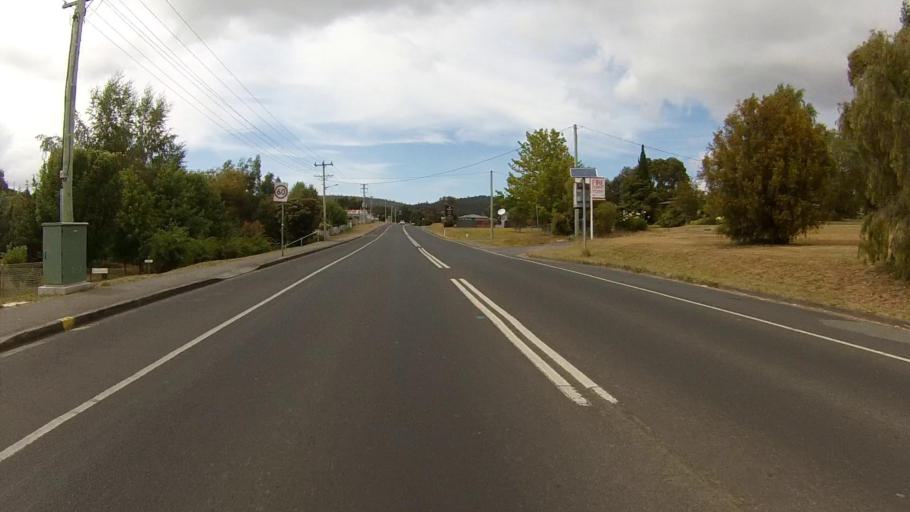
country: AU
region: Tasmania
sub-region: Kingborough
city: Margate
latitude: -43.0668
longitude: 147.2555
